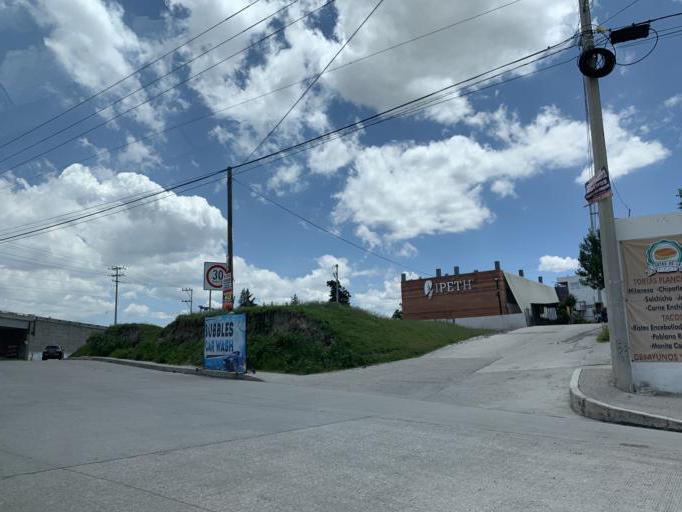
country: MX
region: Puebla
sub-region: Puebla
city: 18 de Marzo
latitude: 18.9703
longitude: -98.1985
